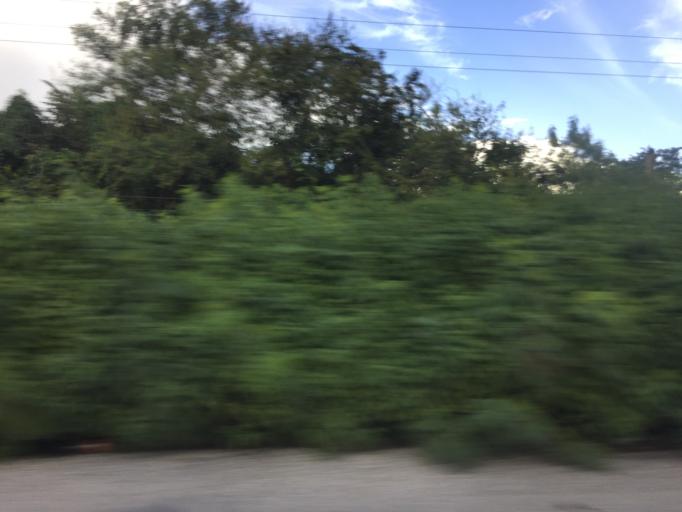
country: MX
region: Quintana Roo
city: Tulum
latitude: 20.2735
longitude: -87.4850
